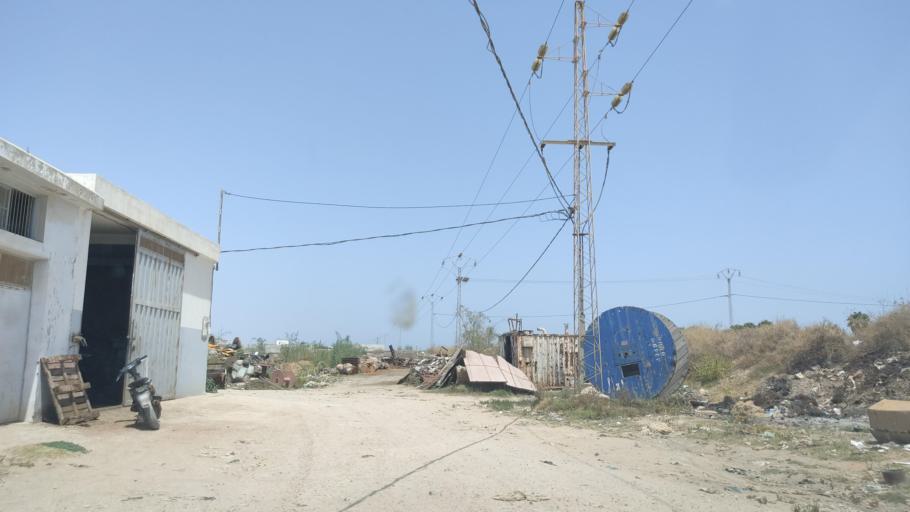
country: TN
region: Safaqis
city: Sfax
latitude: 34.7096
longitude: 10.7311
